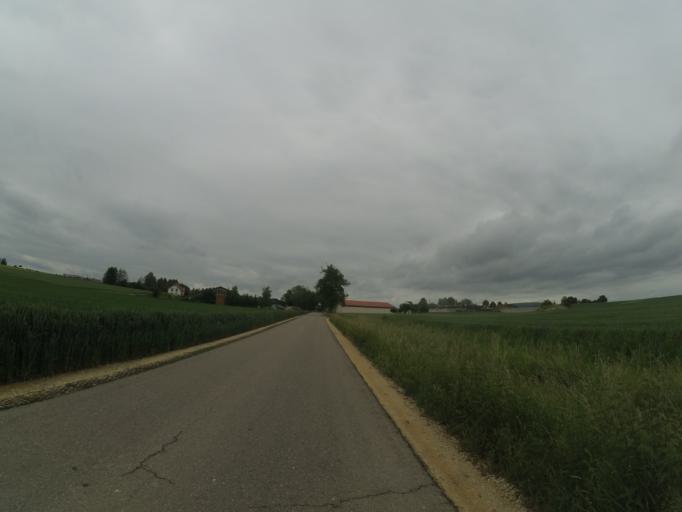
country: DE
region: Baden-Wuerttemberg
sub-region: Tuebingen Region
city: Langenau
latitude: 48.4990
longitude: 10.0925
